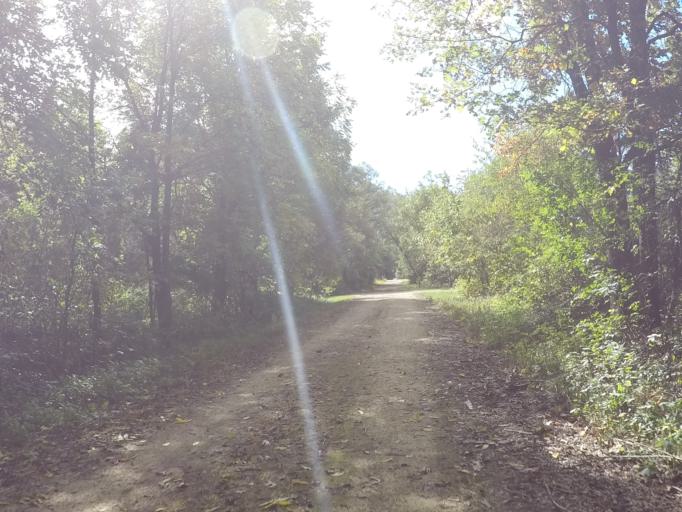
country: US
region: Wisconsin
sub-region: Richland County
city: Richland Center
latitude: 43.2247
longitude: -90.2974
